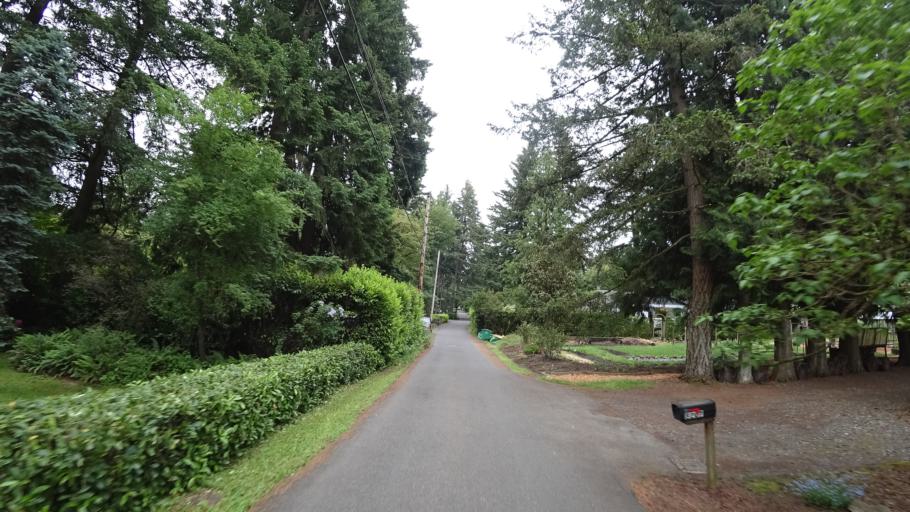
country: US
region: Oregon
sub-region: Washington County
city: Garden Home-Whitford
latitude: 45.4653
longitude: -122.7323
